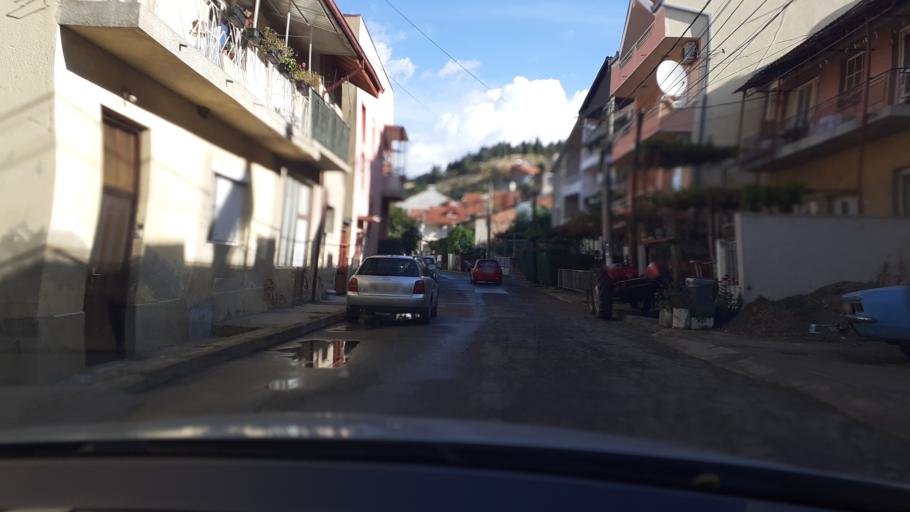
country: MK
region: Kocani
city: Kochani
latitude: 41.9222
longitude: 22.4113
